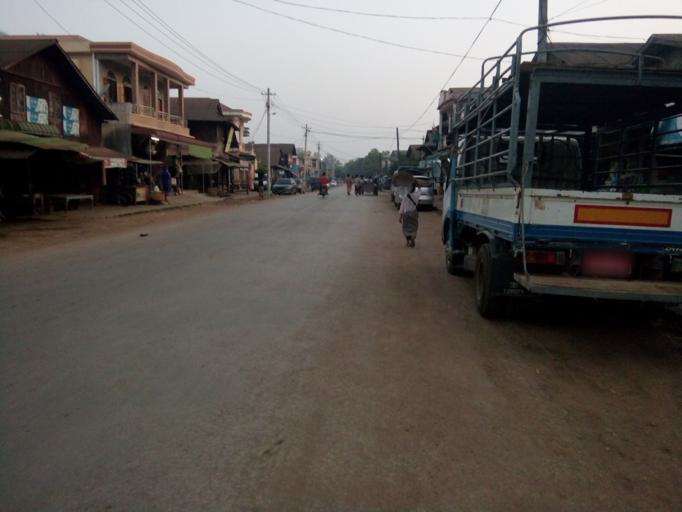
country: MM
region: Kayin
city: Hpa-an
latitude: 17.1216
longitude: 97.8193
